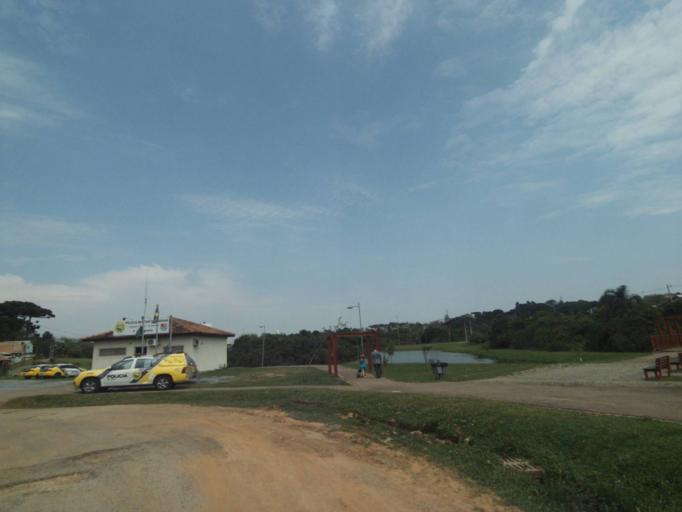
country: BR
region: Parana
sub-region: Curitiba
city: Curitiba
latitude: -25.4730
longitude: -49.3221
